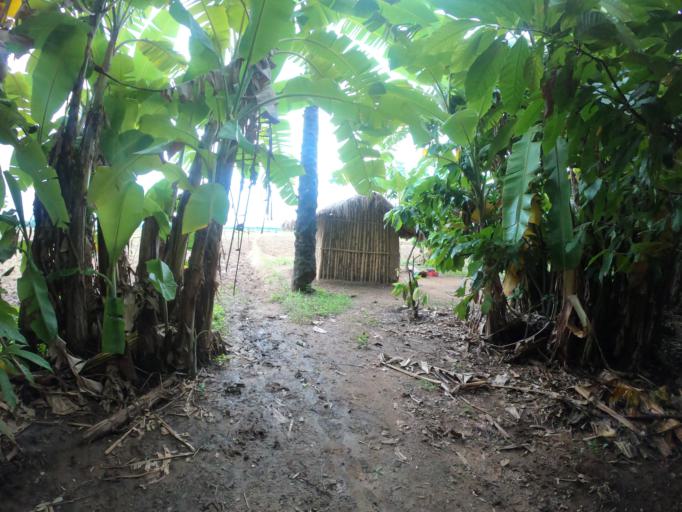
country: TZ
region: Mbeya
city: Kyela
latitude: -9.6588
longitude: 33.8368
